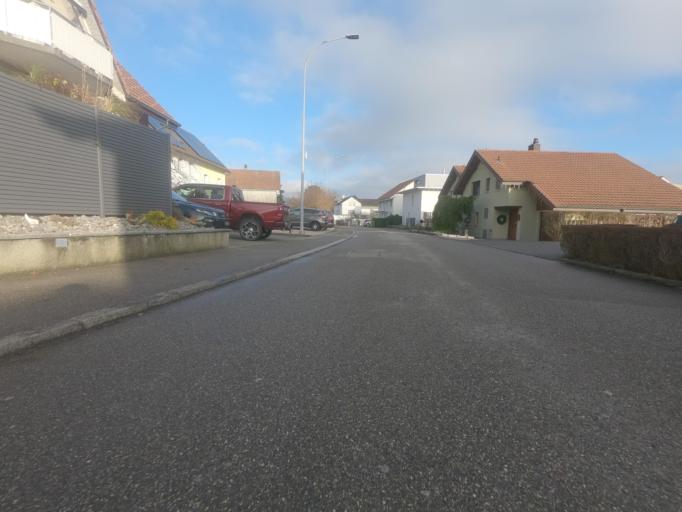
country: CH
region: Solothurn
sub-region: Bezirk Lebern
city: Bettlach
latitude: 47.2002
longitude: 7.4269
